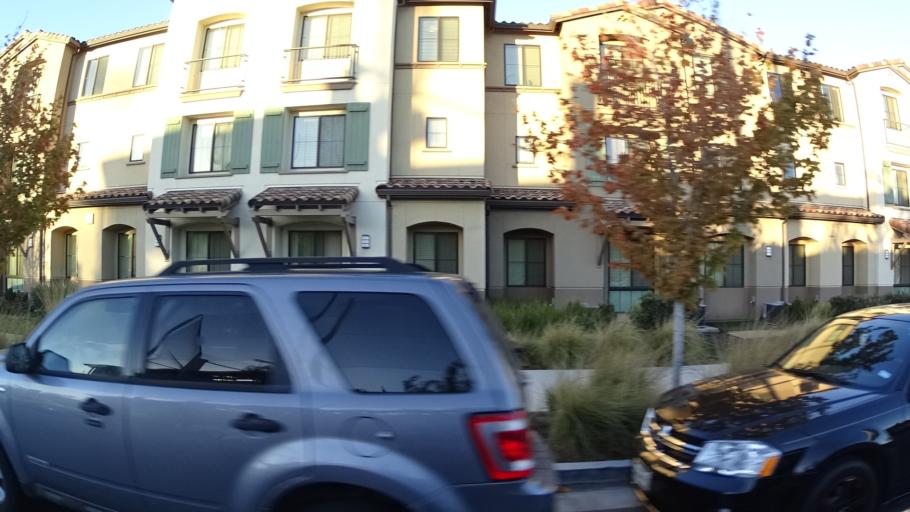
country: US
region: California
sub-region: Santa Clara County
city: Santa Clara
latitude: 37.3491
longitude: -121.9314
